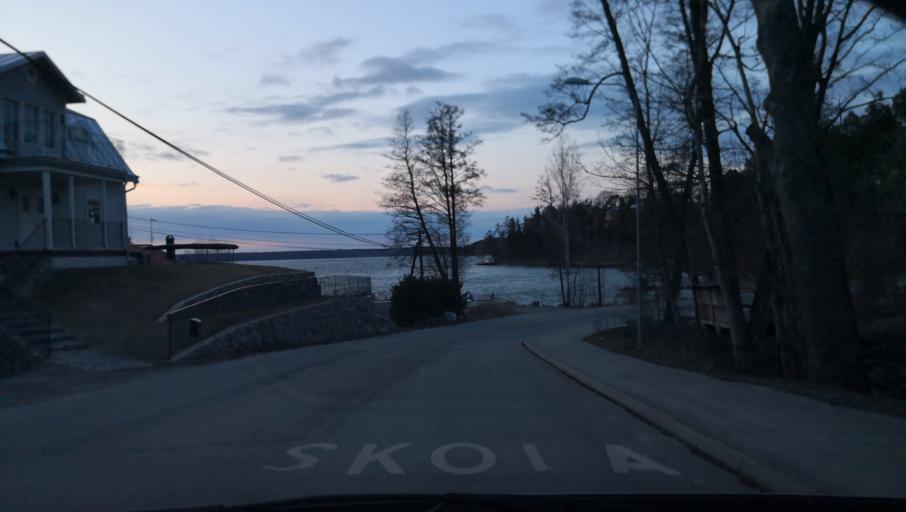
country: SE
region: Stockholm
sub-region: Nacka Kommun
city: Kummelnas
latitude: 59.3566
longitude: 18.2944
